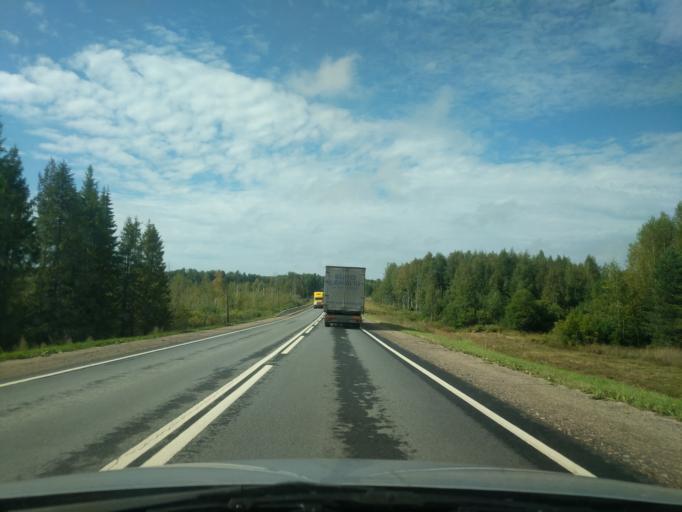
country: RU
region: Kostroma
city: Sudislavl'
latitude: 57.8431
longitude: 41.8336
